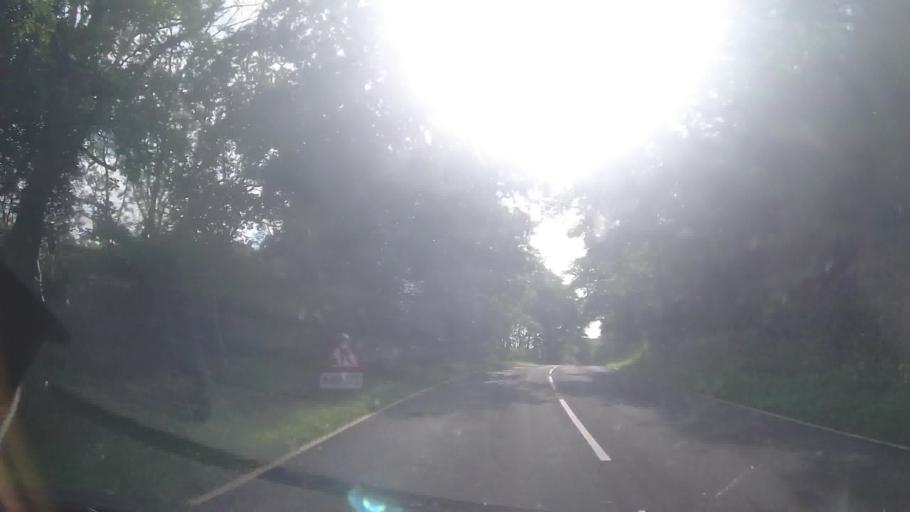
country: GB
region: Wales
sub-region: Gwynedd
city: Barmouth
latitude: 52.7419
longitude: -4.0059
